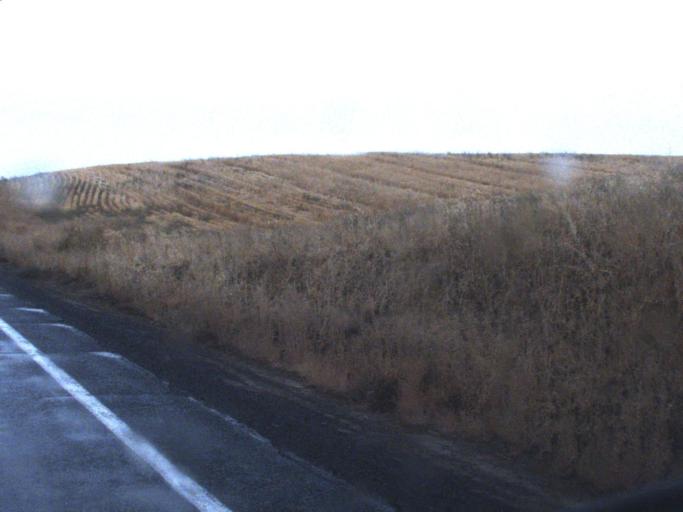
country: US
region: Washington
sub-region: Lincoln County
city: Davenport
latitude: 47.4781
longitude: -118.2069
